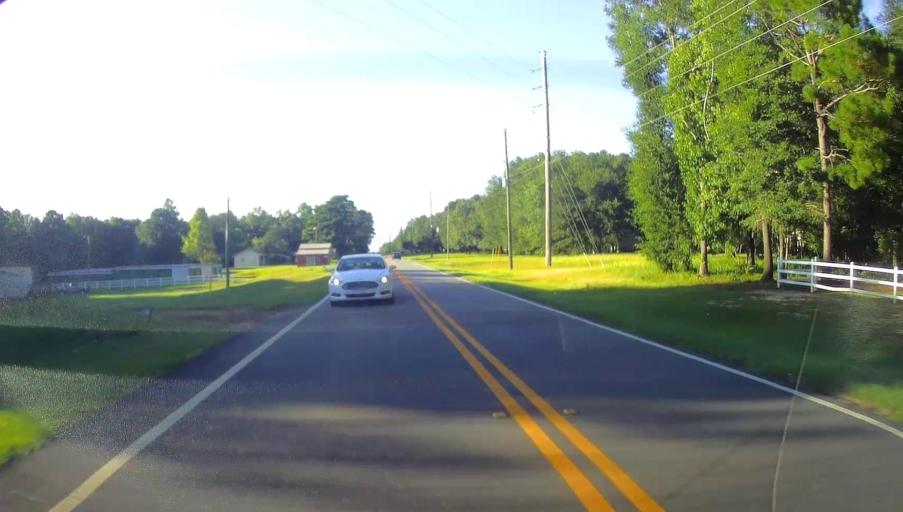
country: US
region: Georgia
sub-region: Pulaski County
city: Hawkinsville
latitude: 32.2902
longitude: -83.4491
